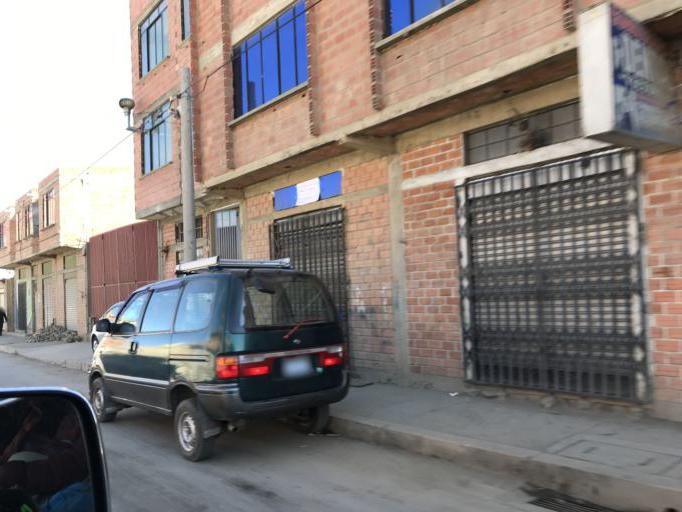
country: BO
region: La Paz
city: La Paz
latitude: -16.4867
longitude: -68.1850
